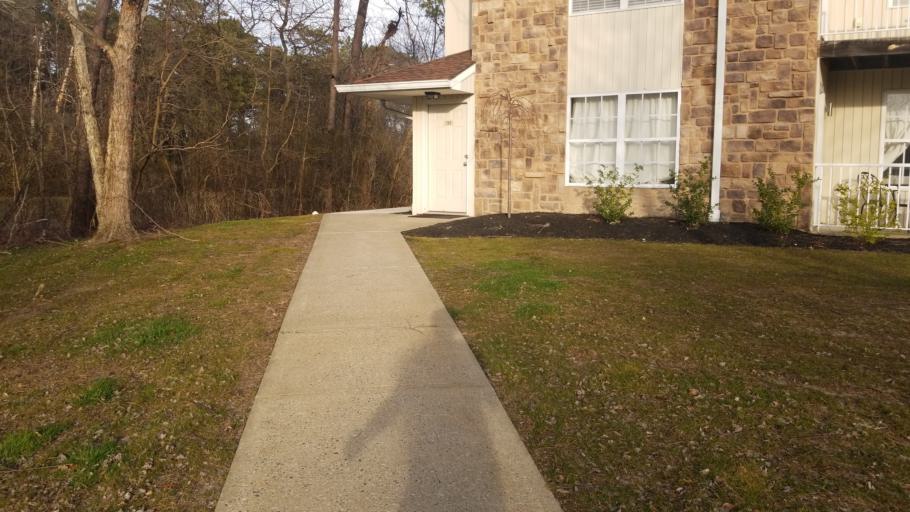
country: US
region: New Jersey
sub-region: Ocean County
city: Leisure Knoll
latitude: 39.9997
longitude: -74.2901
